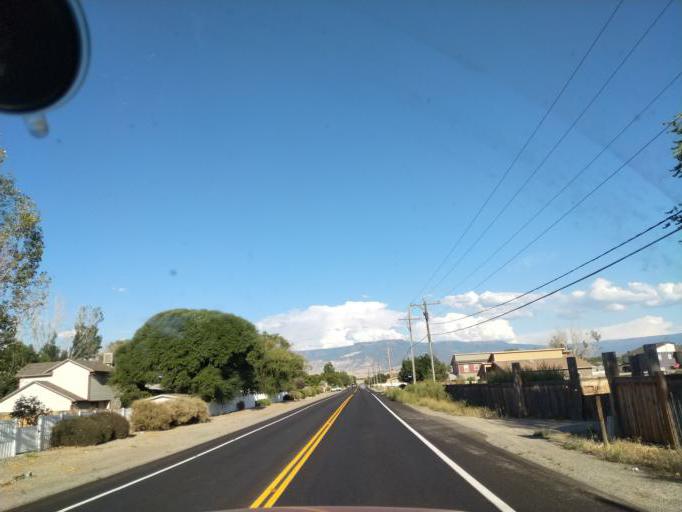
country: US
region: Colorado
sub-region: Mesa County
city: Fruitvale
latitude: 39.0629
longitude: -108.4712
